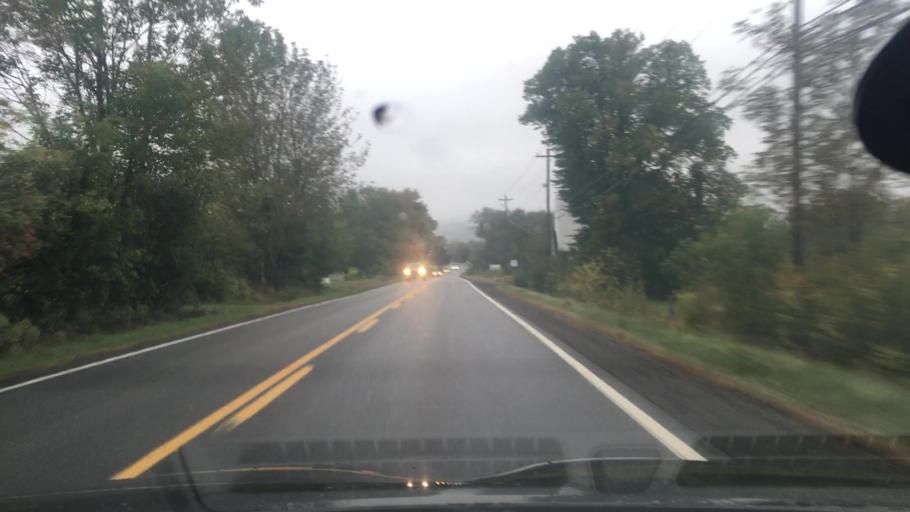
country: CA
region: Nova Scotia
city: Windsor
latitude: 44.9444
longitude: -64.1825
